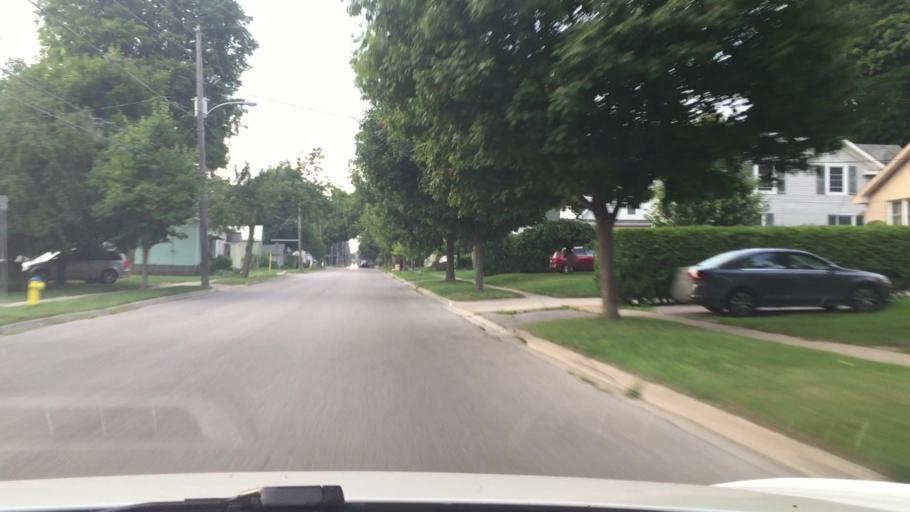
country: CA
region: Ontario
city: Cobourg
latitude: 43.9569
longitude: -78.2890
